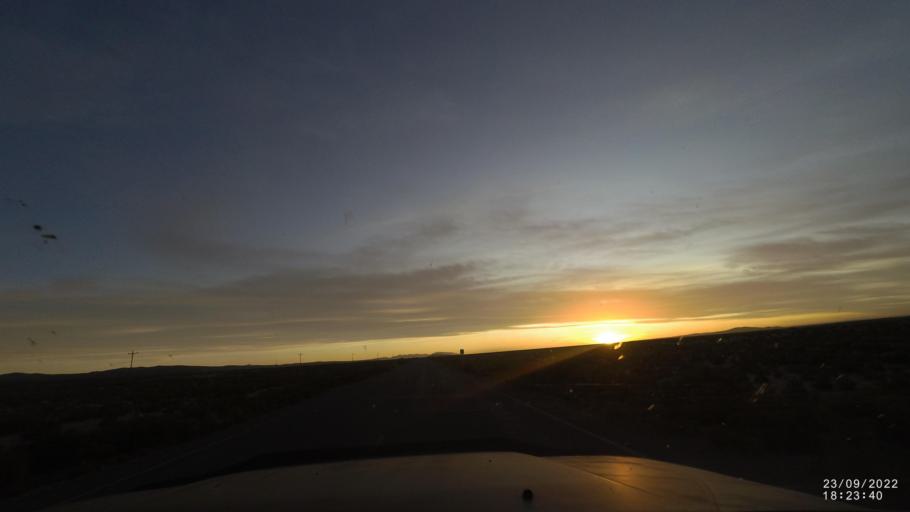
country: BO
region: Oruro
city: Challapata
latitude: -19.2968
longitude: -67.1073
